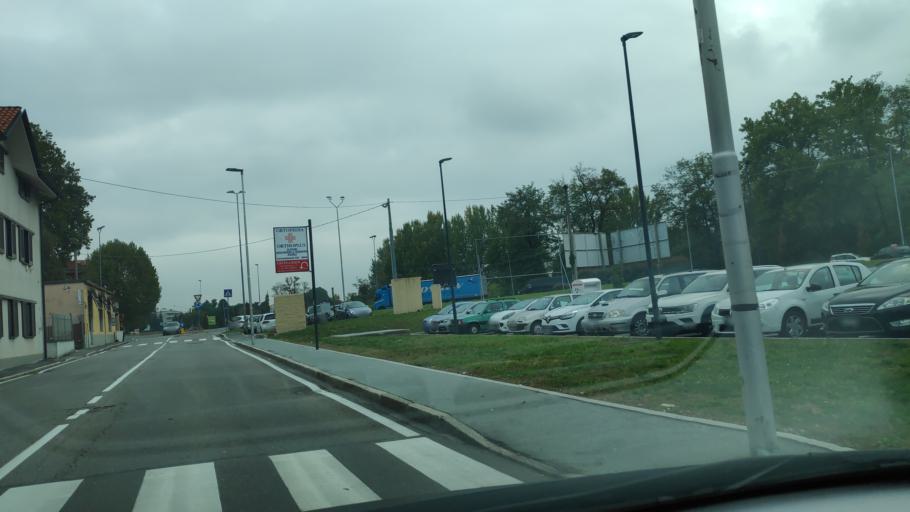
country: IT
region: Lombardy
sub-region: Provincia di Varese
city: Castellanza
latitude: 45.6080
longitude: 8.9083
